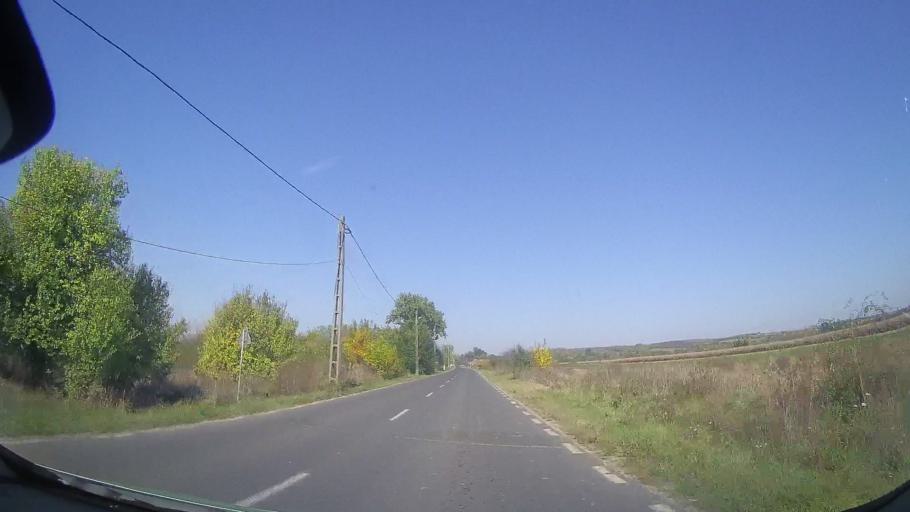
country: RO
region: Timis
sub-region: Comuna Balint
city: Balint
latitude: 45.8055
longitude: 21.8611
